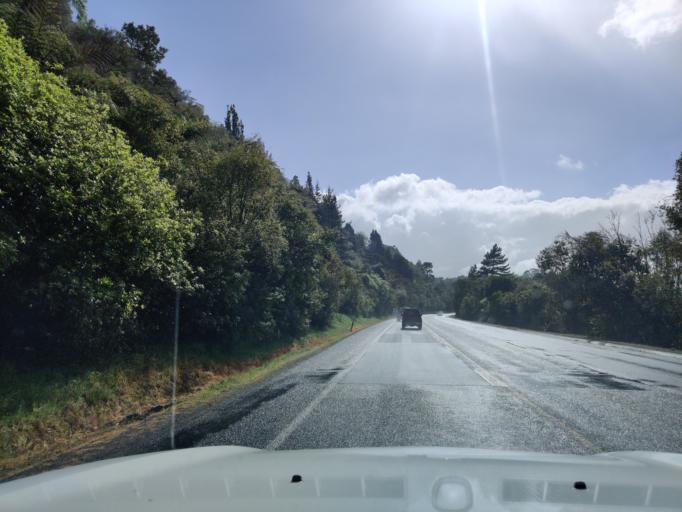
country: NZ
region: Waikato
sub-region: Matamata-Piako District
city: Matamata
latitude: -37.9484
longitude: 175.6397
